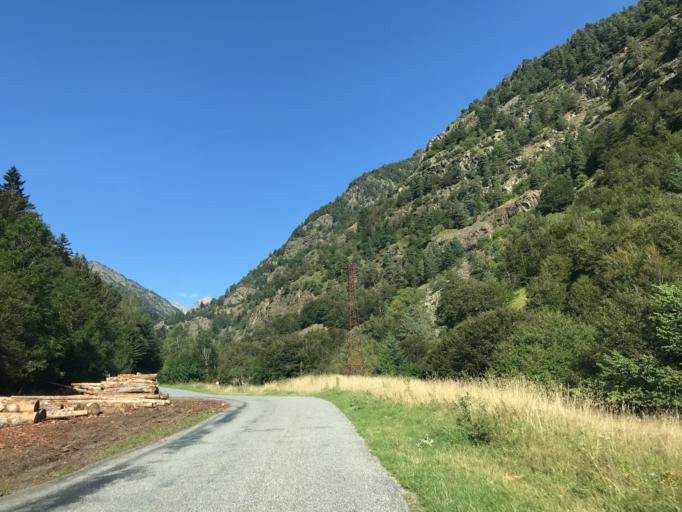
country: FR
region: Midi-Pyrenees
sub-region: Departement des Hautes-Pyrenees
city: Saint-Lary-Soulan
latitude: 42.8143
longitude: 0.2140
